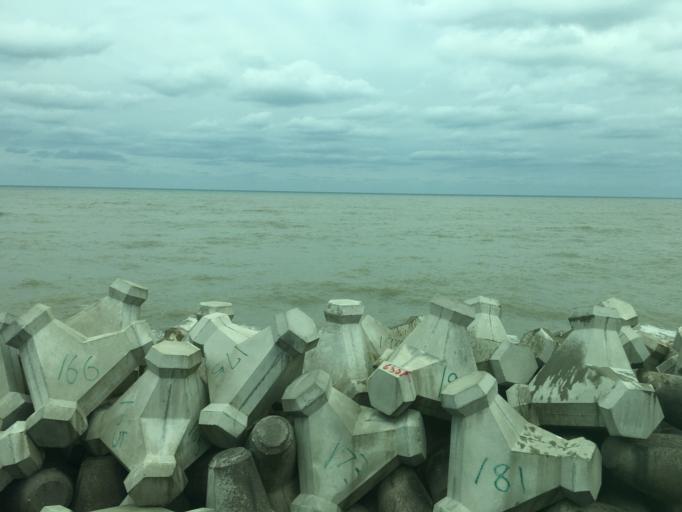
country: JP
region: Aomori
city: Shimokizukuri
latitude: 40.6803
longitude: 139.9614
